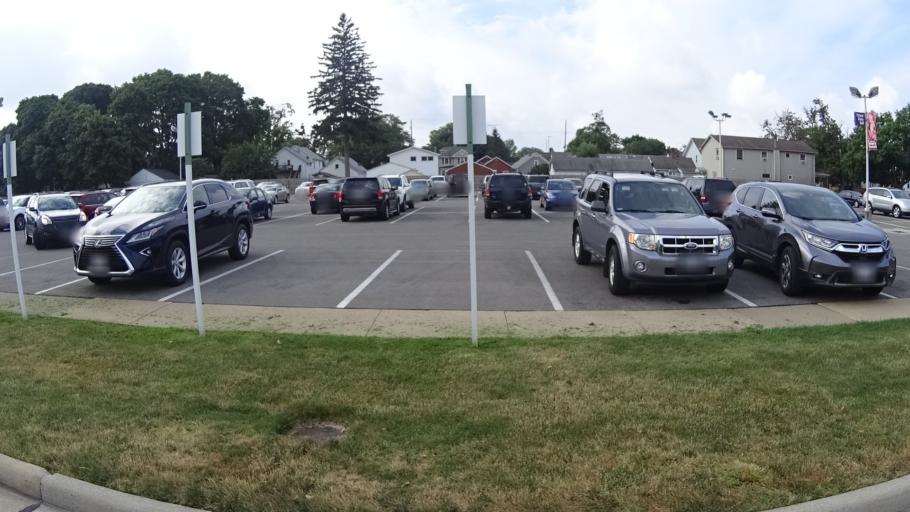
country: US
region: Ohio
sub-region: Erie County
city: Sandusky
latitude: 41.4447
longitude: -82.7118
